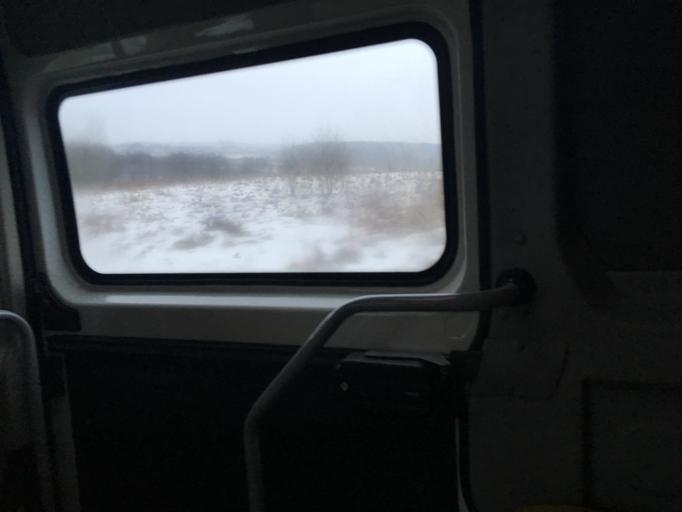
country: RU
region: Tula
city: Dubna
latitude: 54.0918
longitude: 37.0801
